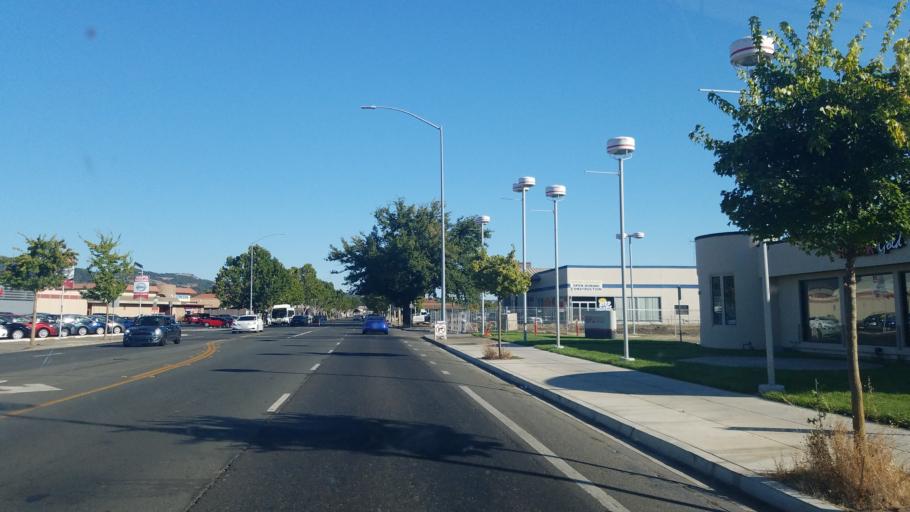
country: US
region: California
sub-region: Napa County
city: Napa
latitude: 38.2931
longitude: -122.2785
